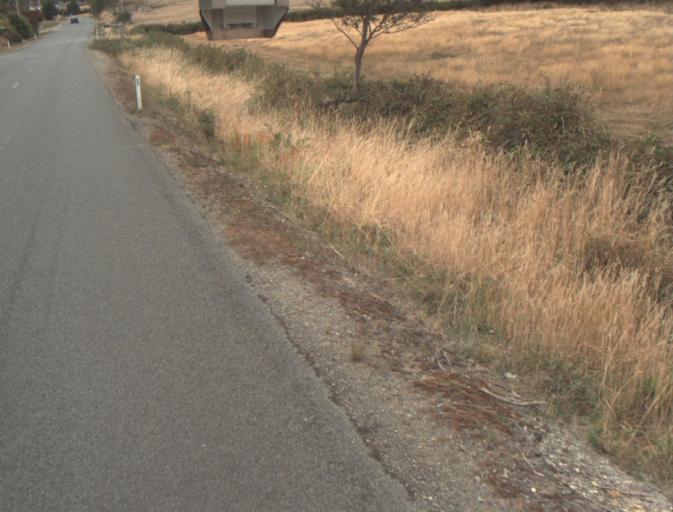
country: AU
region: Tasmania
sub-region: Launceston
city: Mayfield
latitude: -41.1983
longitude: 147.2183
